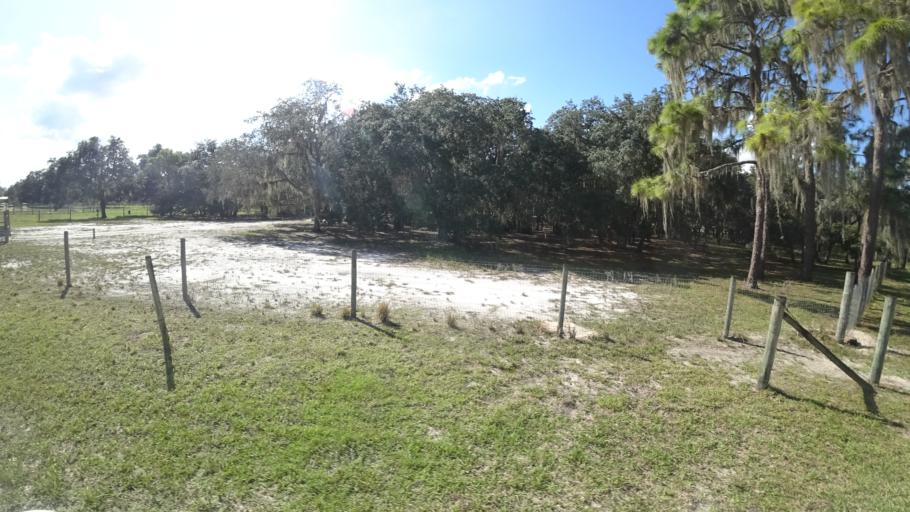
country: US
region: Florida
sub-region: Hardee County
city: Wauchula
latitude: 27.4836
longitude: -82.0554
